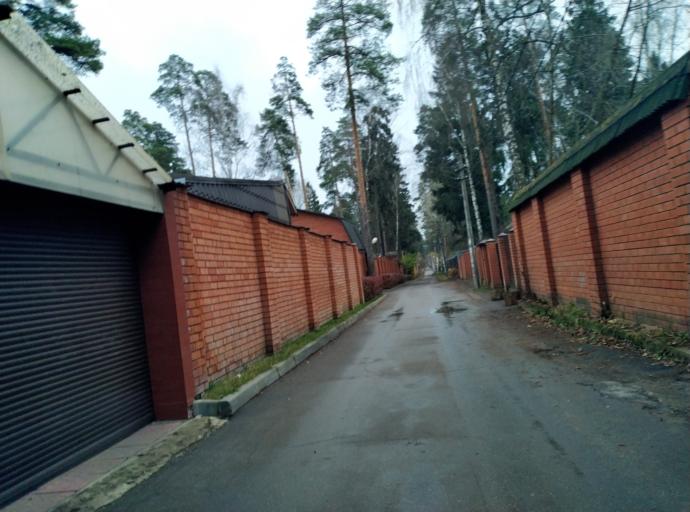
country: RU
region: Moskovskaya
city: Korenevo
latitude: 55.6583
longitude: 38.0007
